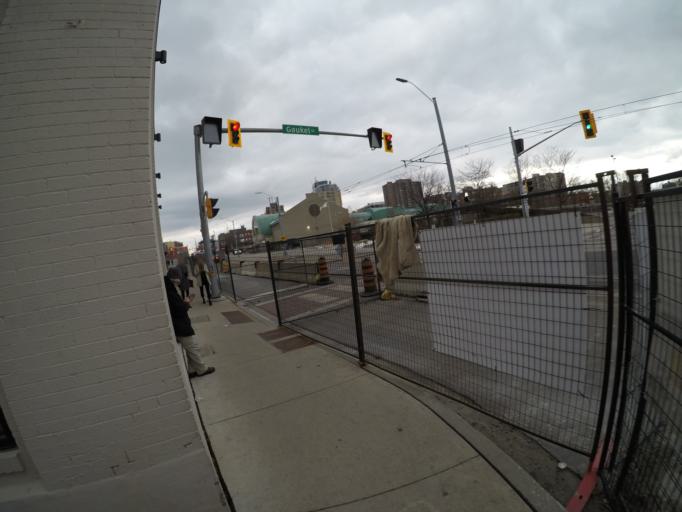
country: CA
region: Ontario
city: Waterloo
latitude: 43.4502
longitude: -80.4930
